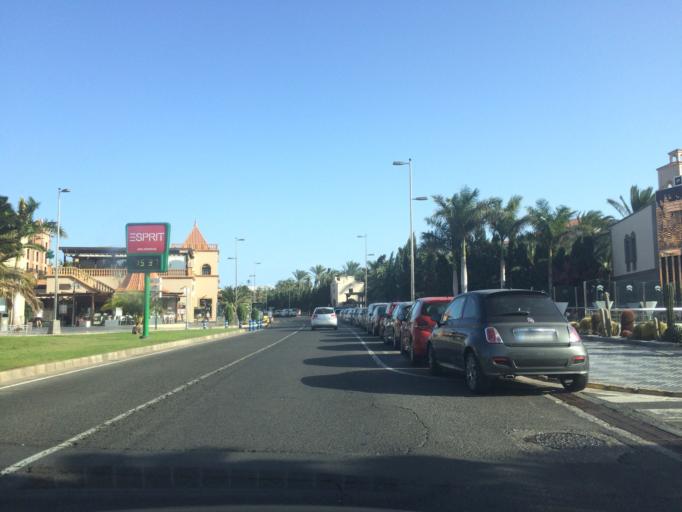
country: ES
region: Canary Islands
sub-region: Provincia de Las Palmas
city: Maspalomas
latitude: 27.7395
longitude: -15.6009
